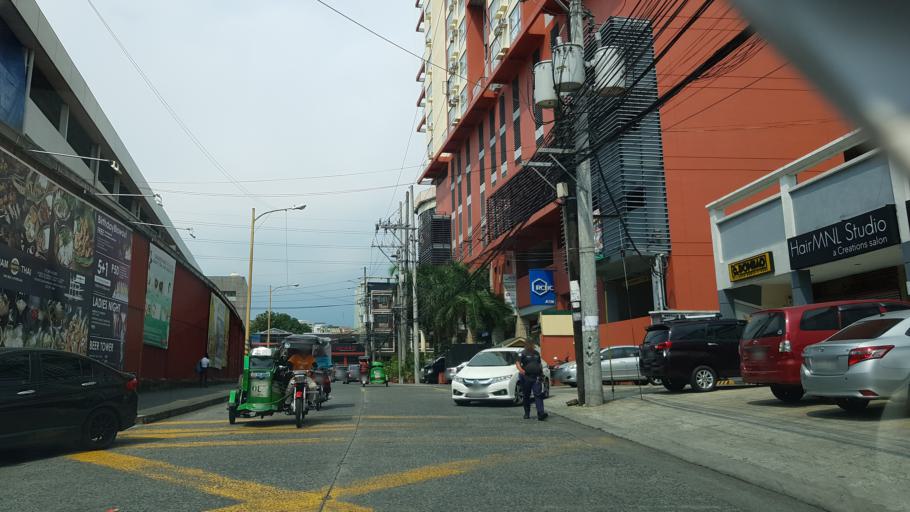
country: PH
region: Metro Manila
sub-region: Pasig
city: Pasig City
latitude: 14.5729
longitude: 121.0582
